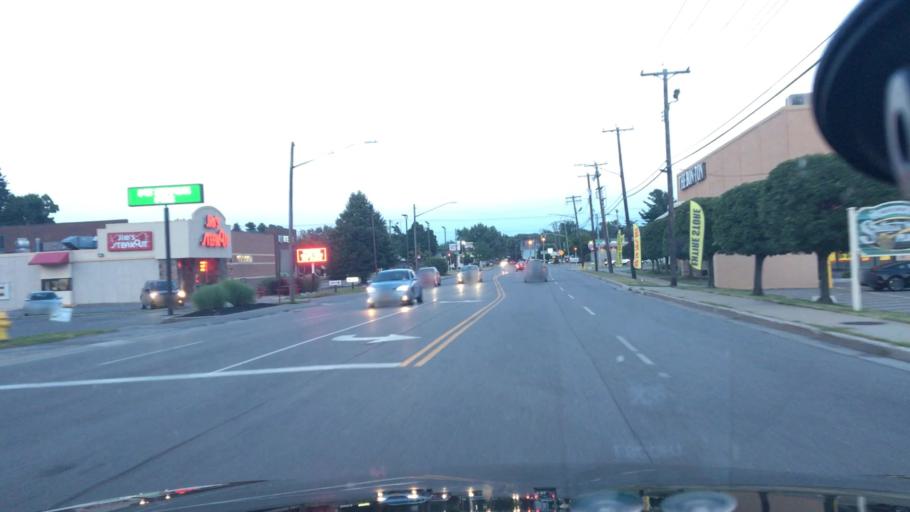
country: US
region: New York
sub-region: Erie County
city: West Seneca
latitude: 42.8301
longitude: -78.7557
